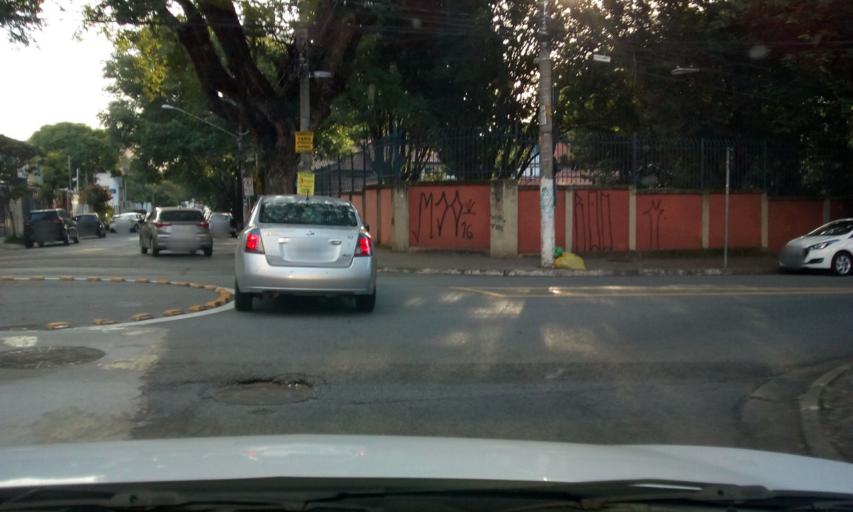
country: BR
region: Sao Paulo
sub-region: Sao Paulo
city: Sao Paulo
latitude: -23.5292
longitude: -46.6942
